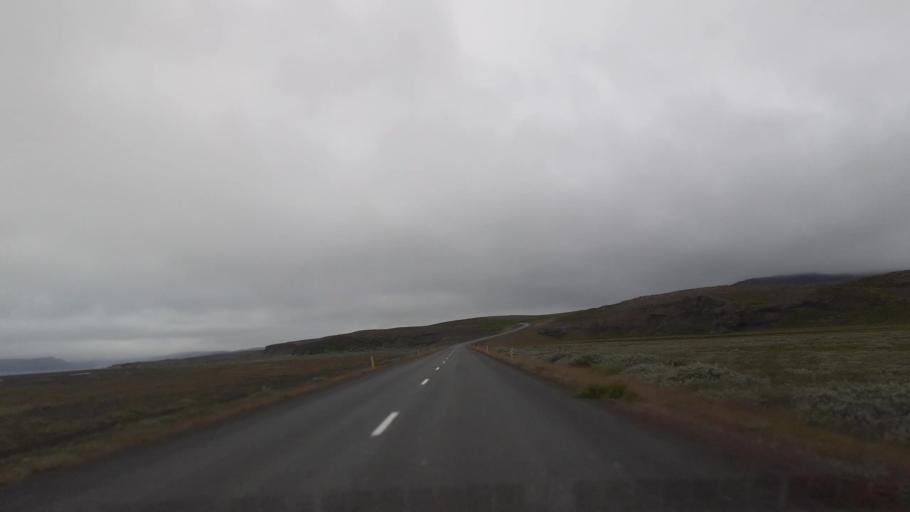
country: IS
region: Northeast
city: Husavik
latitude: 66.2029
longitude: -16.4732
